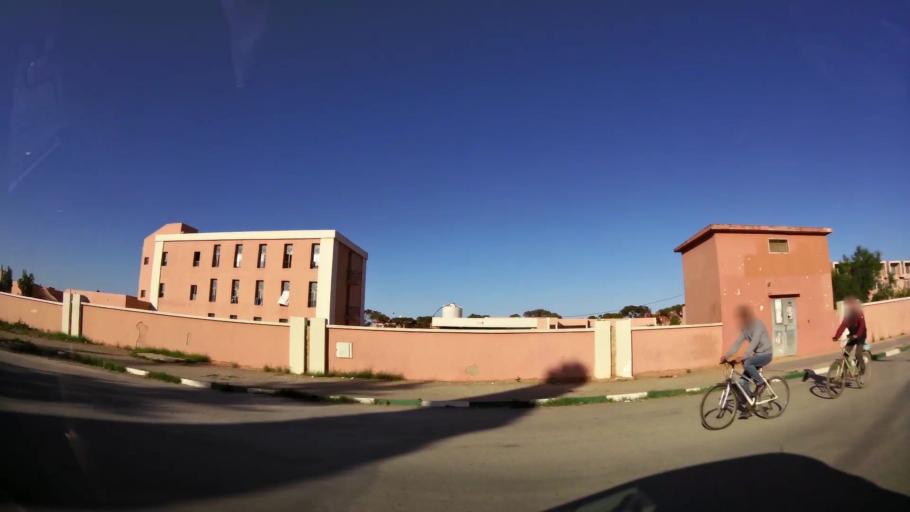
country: MA
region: Oriental
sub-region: Berkane-Taourirt
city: Berkane
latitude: 34.9301
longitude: -2.3193
